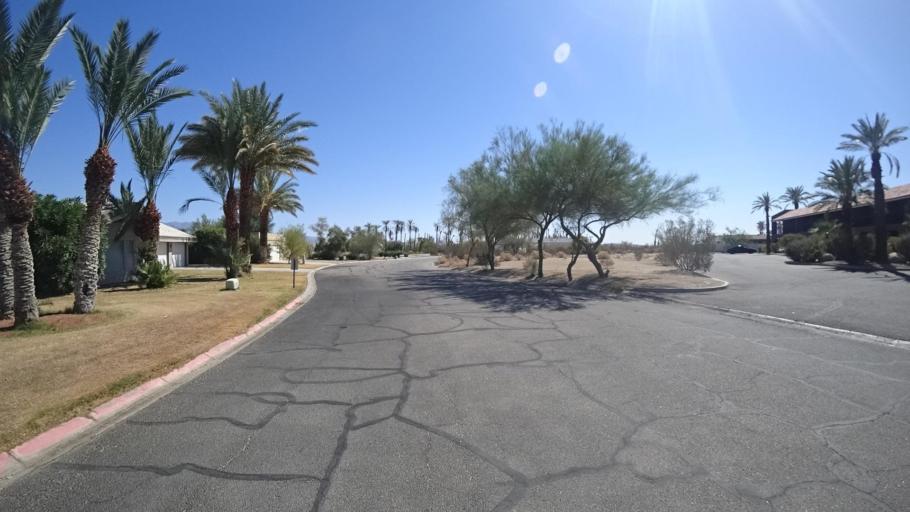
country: US
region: California
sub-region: San Diego County
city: Borrego Springs
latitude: 33.2379
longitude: -116.3550
